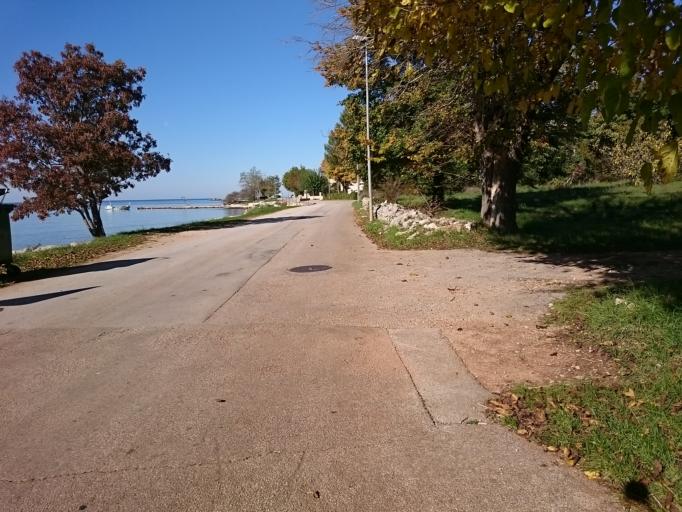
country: HR
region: Istarska
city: Umag
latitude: 45.3790
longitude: 13.5450
